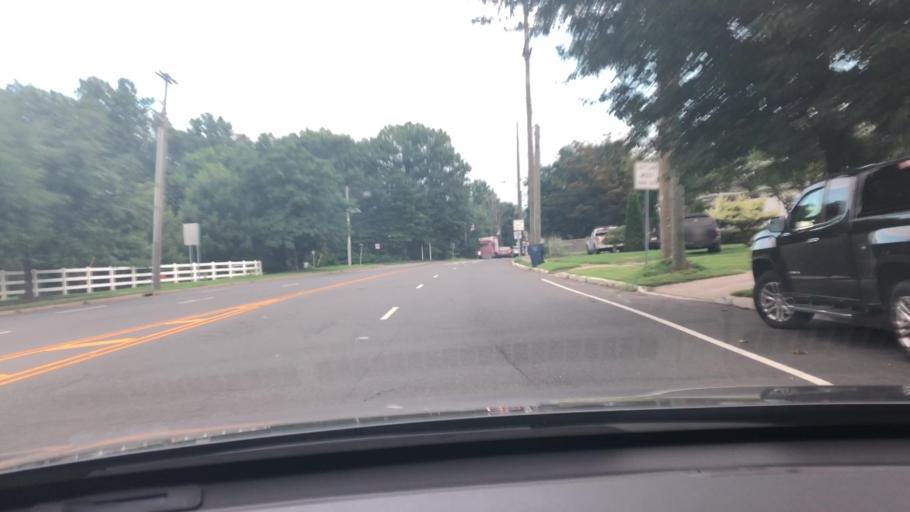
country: US
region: New Jersey
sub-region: Middlesex County
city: Milltown
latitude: 40.4632
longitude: -74.4468
